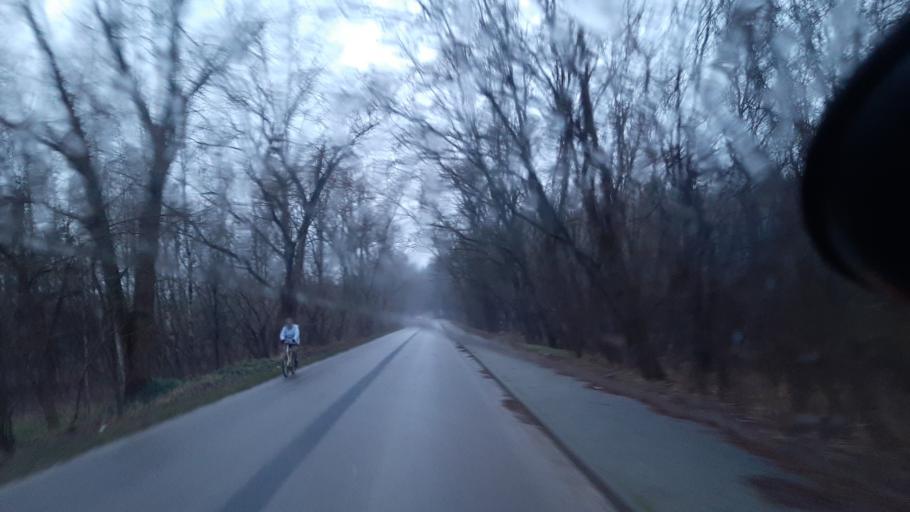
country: PL
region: Lublin Voivodeship
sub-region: Powiat lubartowski
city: Firlej
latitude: 51.5580
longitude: 22.5288
